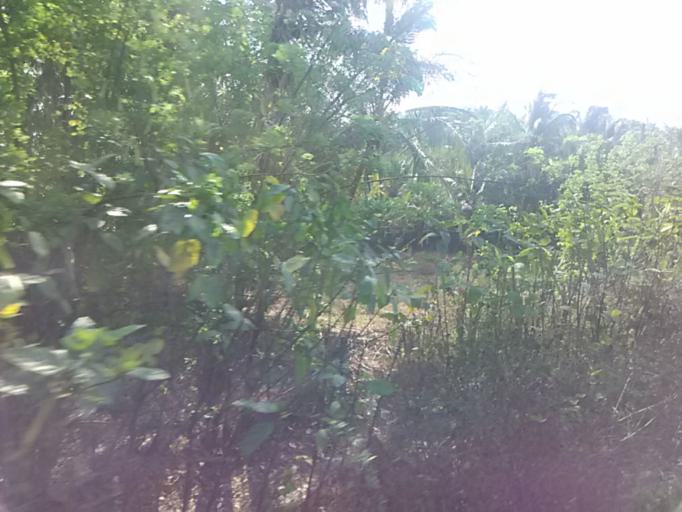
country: IN
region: Kerala
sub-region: Palakkad district
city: Shoranur
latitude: 10.7010
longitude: 76.2631
